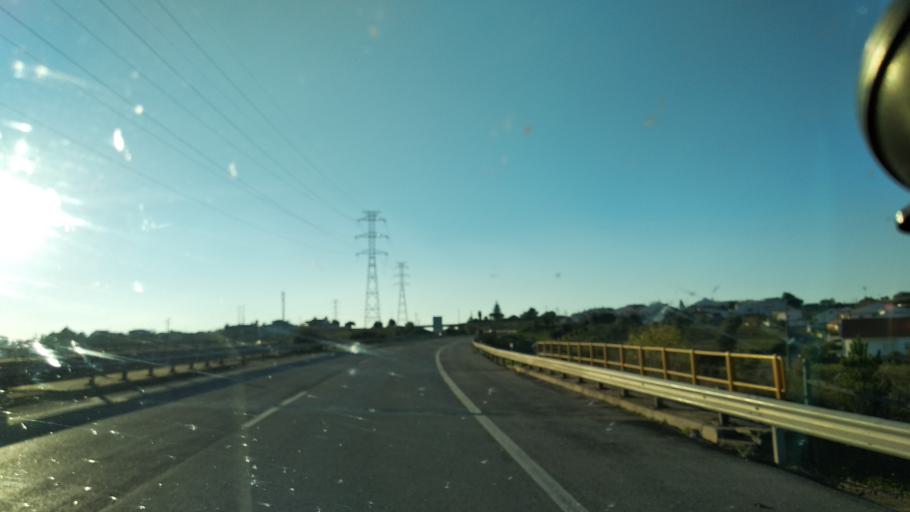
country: PT
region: Santarem
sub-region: Entroncamento
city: Entroncamento
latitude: 39.4713
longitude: -8.4957
